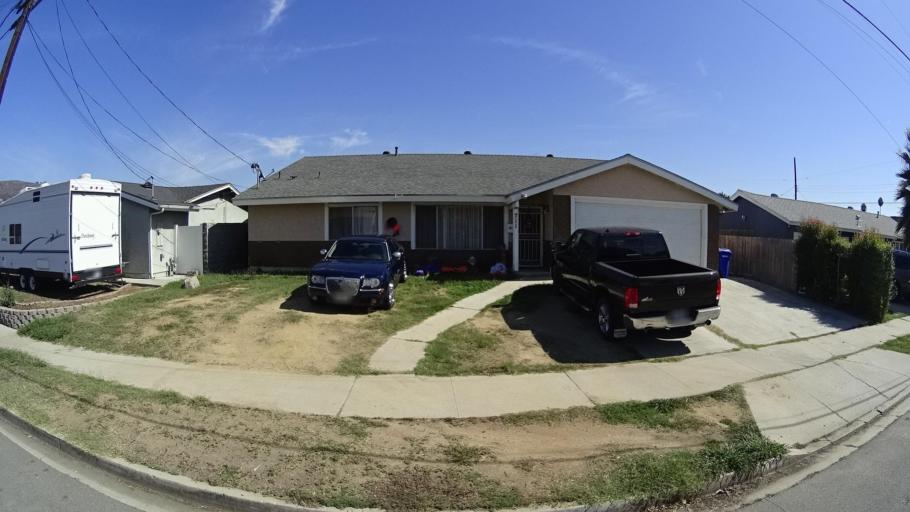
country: US
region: California
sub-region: San Diego County
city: La Presa
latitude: 32.7095
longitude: -117.0044
